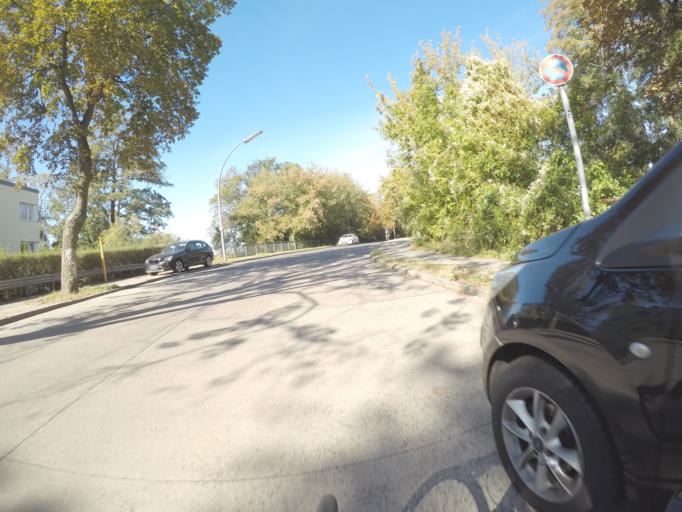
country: DE
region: Berlin
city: Konradshohe
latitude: 52.6015
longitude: 13.2106
